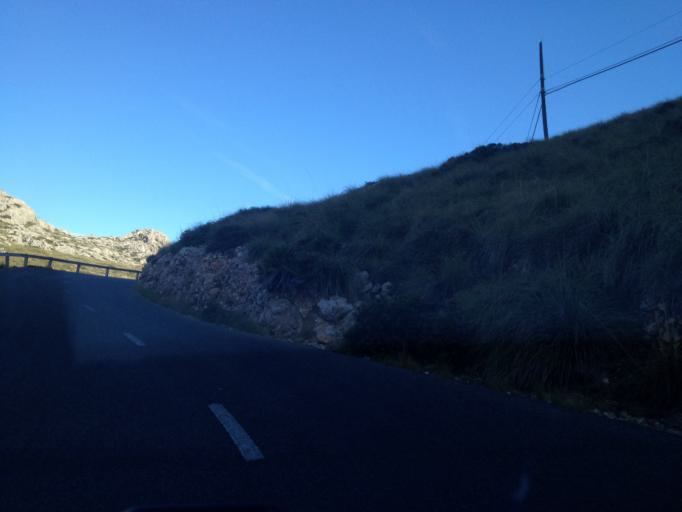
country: ES
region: Balearic Islands
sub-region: Illes Balears
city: Alcudia
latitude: 39.9249
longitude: 3.1084
